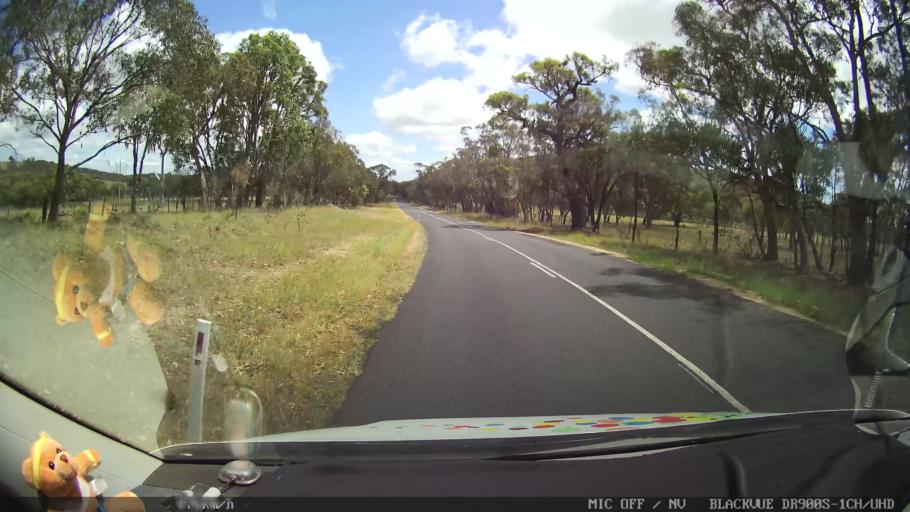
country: AU
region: New South Wales
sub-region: Glen Innes Severn
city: Glen Innes
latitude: -29.5386
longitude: 151.6728
